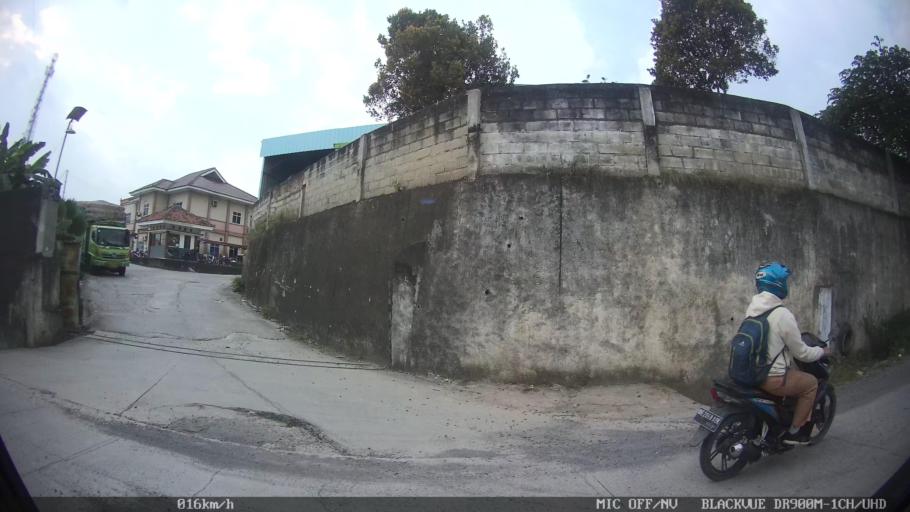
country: ID
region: Lampung
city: Panjang
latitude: -5.4412
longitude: 105.2994
